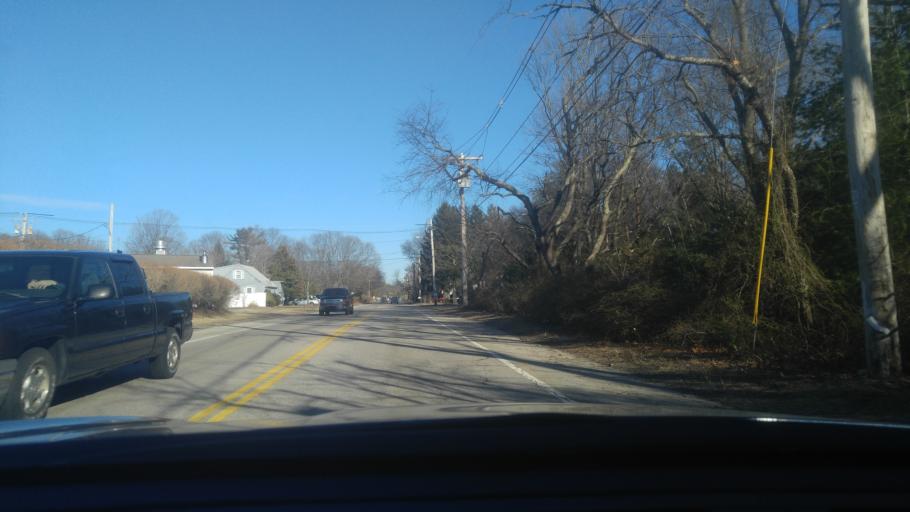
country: US
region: Rhode Island
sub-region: Kent County
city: Warwick
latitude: 41.6984
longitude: -71.4466
